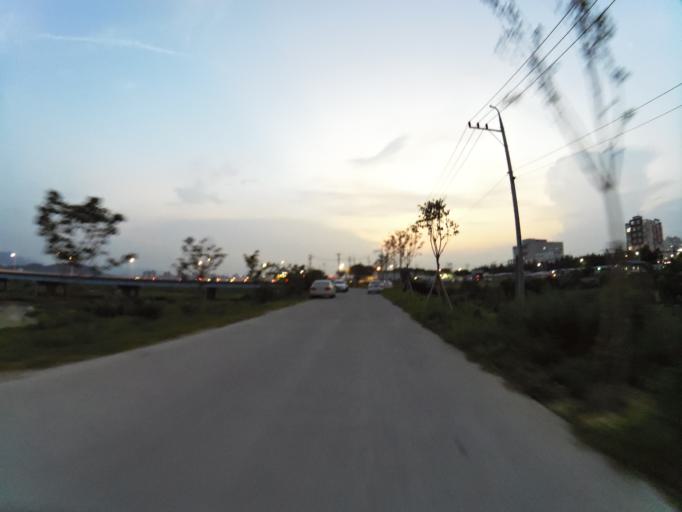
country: KR
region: Gyeongsangbuk-do
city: Gyeongsan-si
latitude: 35.8638
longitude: 128.7162
